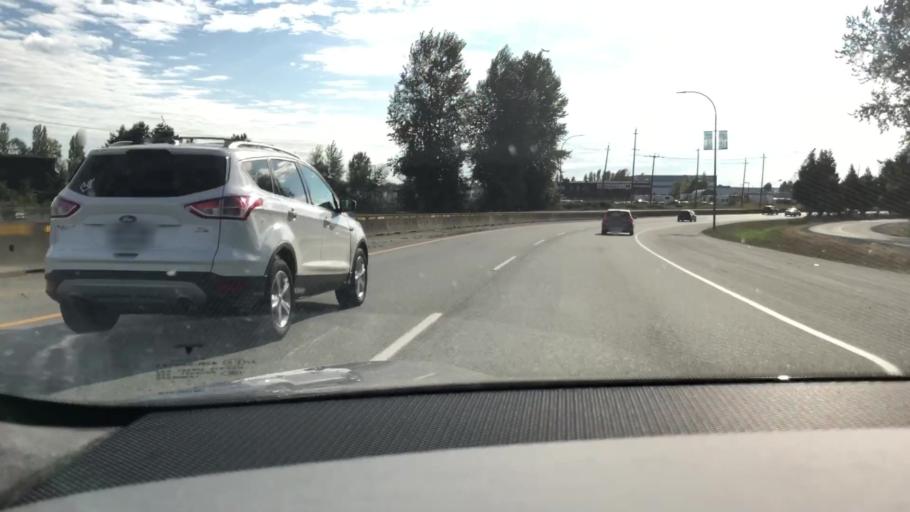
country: CA
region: British Columbia
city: New Westminster
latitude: 49.1960
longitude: -122.9571
